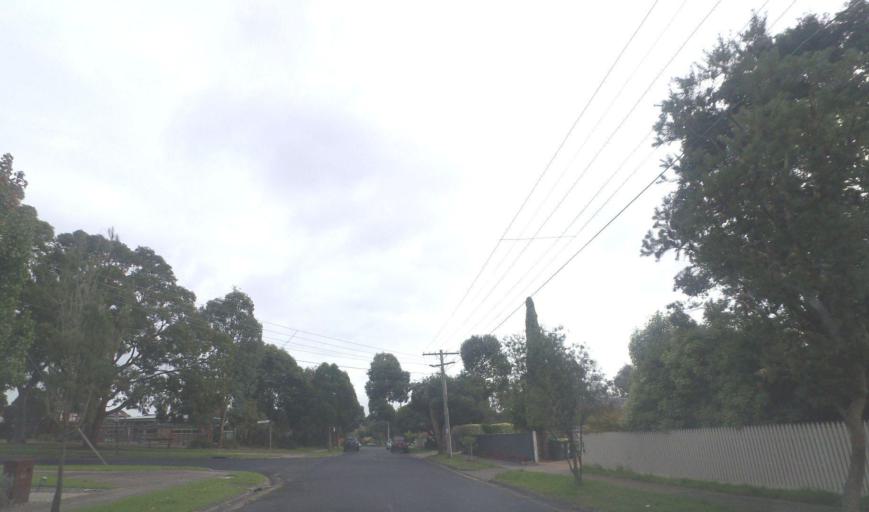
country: AU
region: Victoria
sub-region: Whitehorse
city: Nunawading
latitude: -37.8054
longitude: 145.1719
